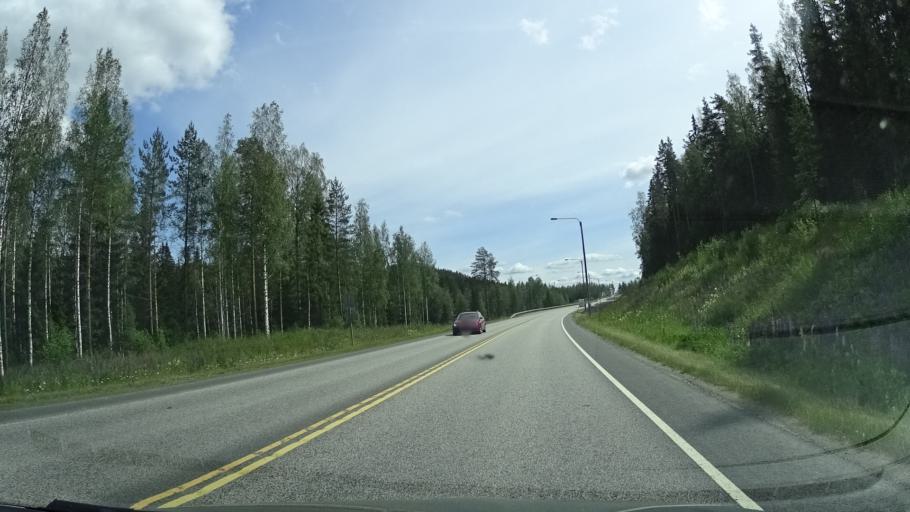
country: FI
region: Central Finland
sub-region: Jyvaeskylae
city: Jyvaeskylae
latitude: 62.2524
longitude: 25.6400
